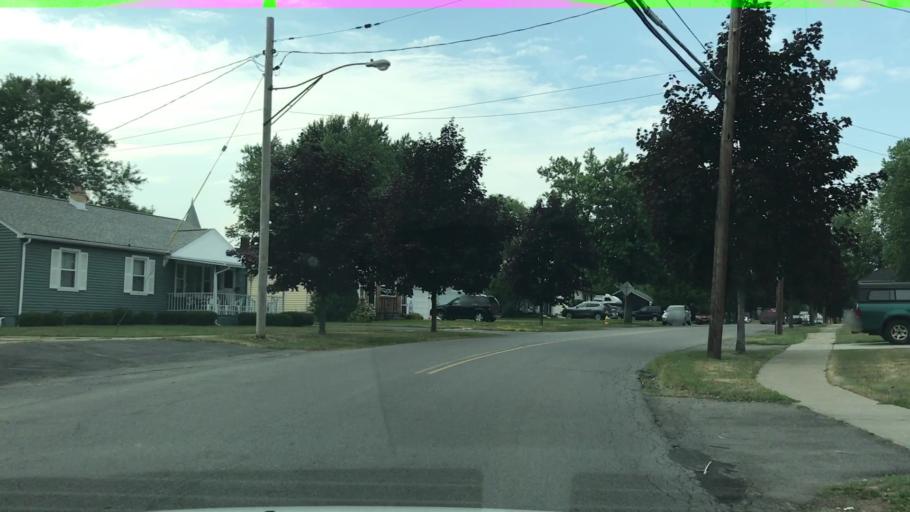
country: US
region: New York
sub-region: Erie County
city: Lancaster
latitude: 42.9064
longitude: -78.6737
